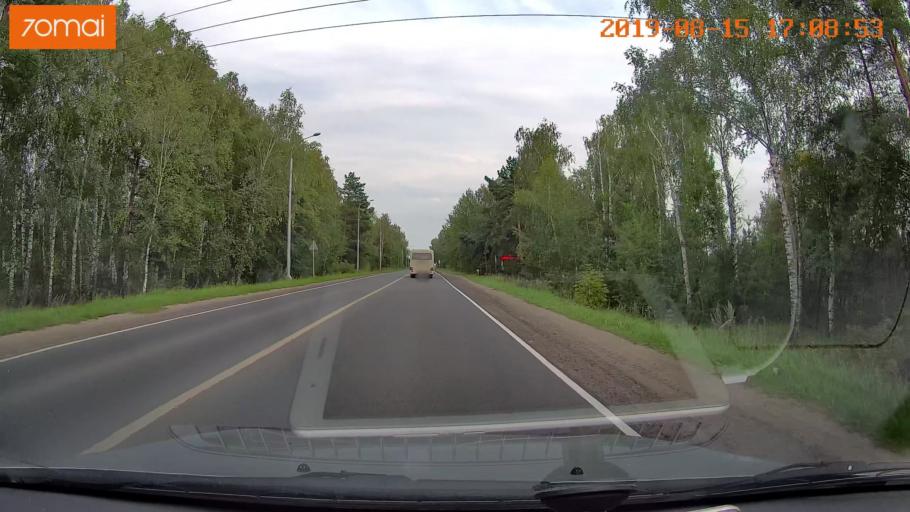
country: RU
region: Moskovskaya
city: Beloozerskiy
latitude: 55.4544
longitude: 38.4313
